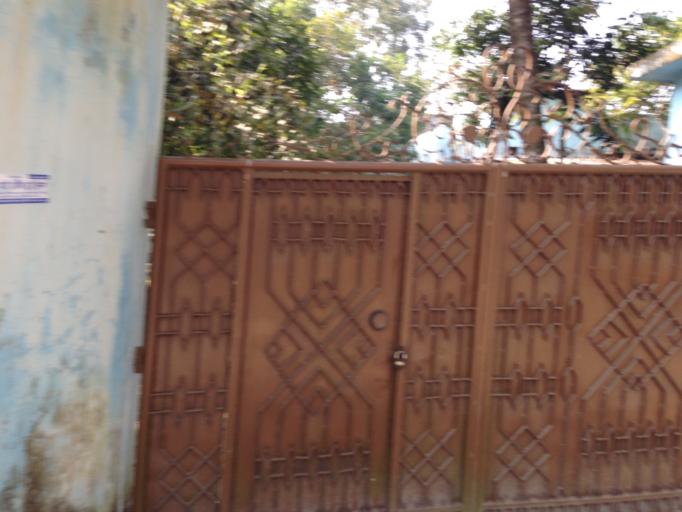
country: BD
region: Chittagong
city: Lakshmipur
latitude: 22.9361
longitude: 90.8333
